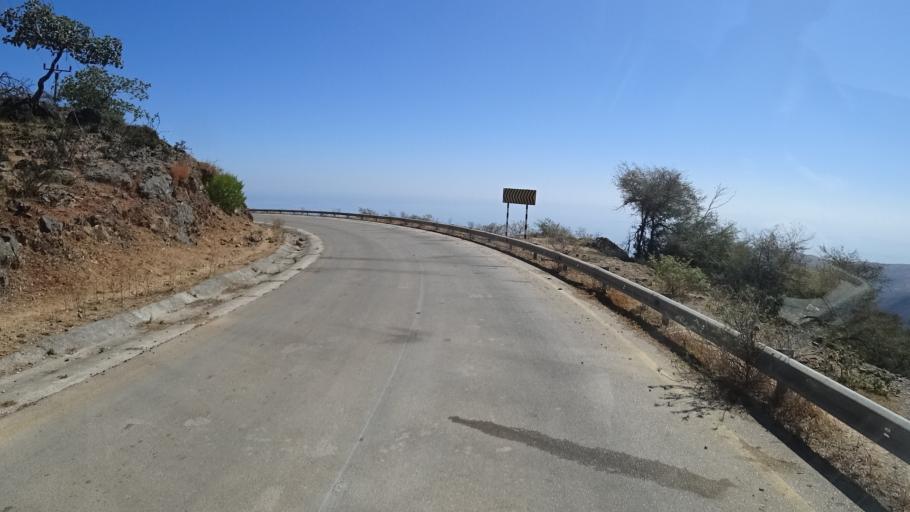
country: YE
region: Al Mahrah
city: Hawf
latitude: 16.7703
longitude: 53.3353
